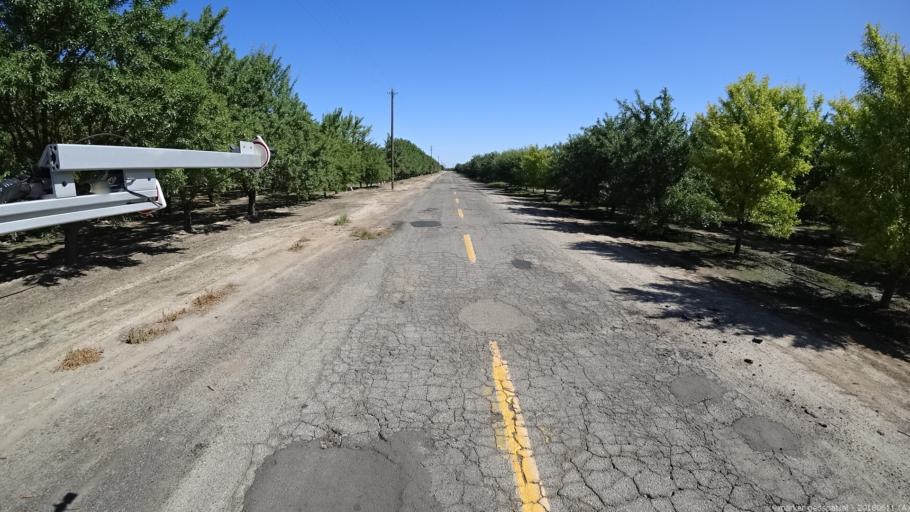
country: US
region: California
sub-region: Madera County
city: Madera
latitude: 36.9605
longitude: -120.1750
